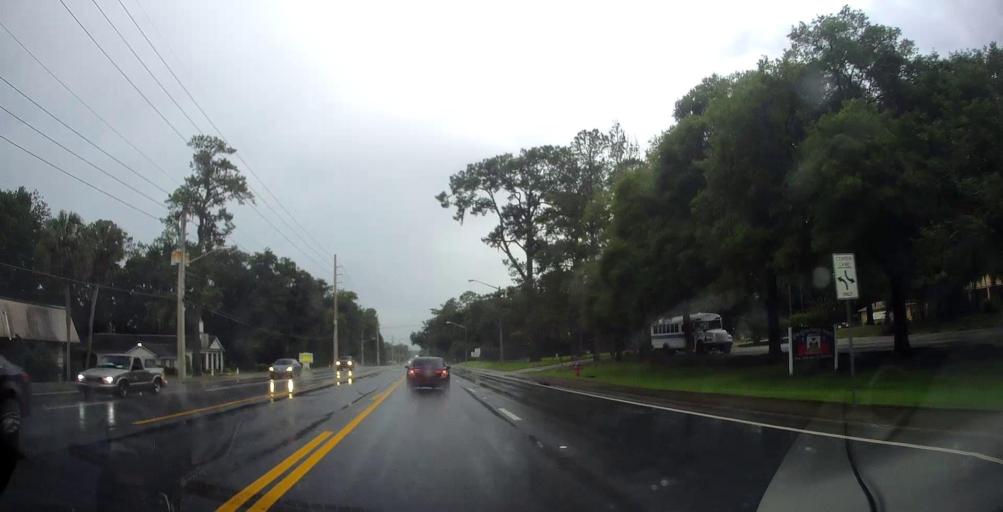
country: US
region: Florida
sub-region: Marion County
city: Ocala
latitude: 29.1855
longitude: -82.0869
